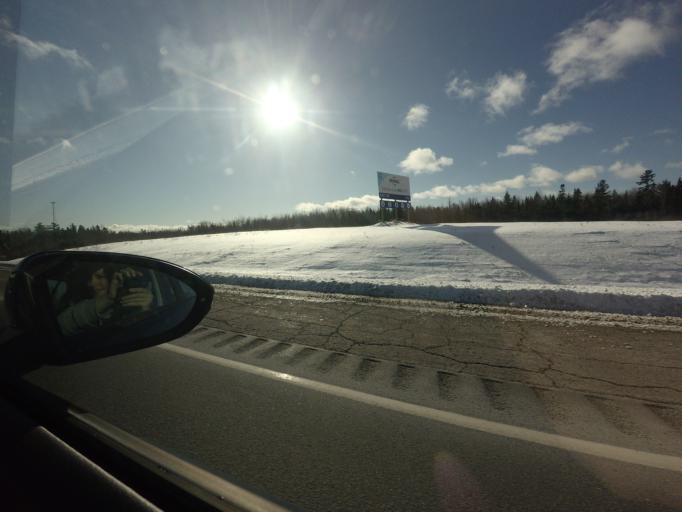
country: CA
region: New Brunswick
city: Fredericton
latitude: 45.8731
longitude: -66.6175
